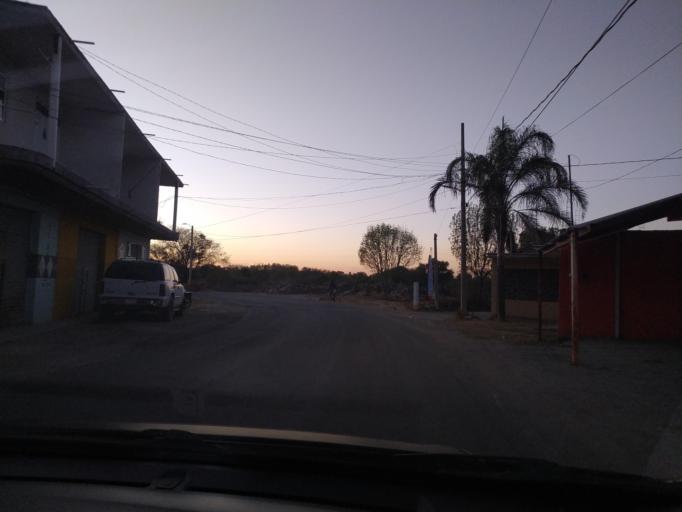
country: MX
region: Guanajuato
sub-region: San Francisco del Rincon
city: San Roque de Montes
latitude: 21.0162
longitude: -101.8162
